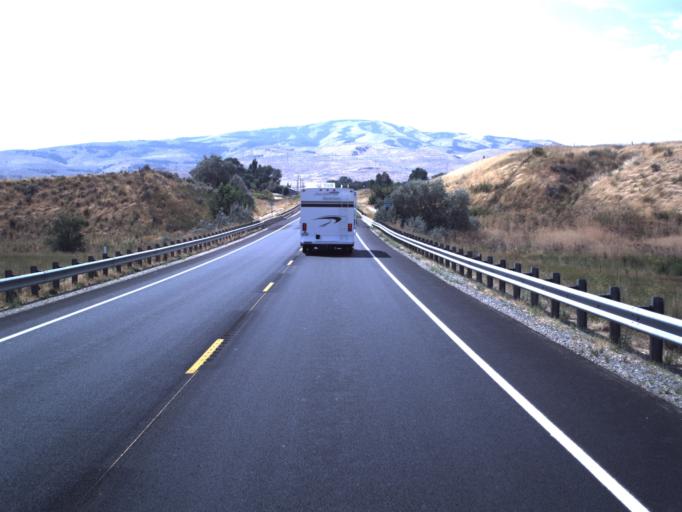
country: US
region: Utah
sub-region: Box Elder County
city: Garland
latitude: 41.7853
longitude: -112.1362
